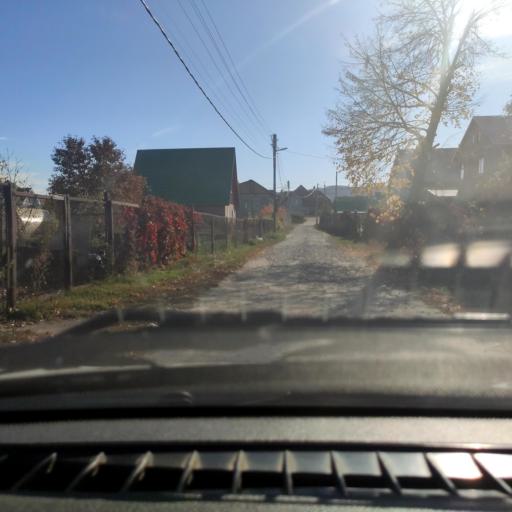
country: RU
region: Samara
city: Zhigulevsk
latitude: 53.4653
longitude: 49.5873
